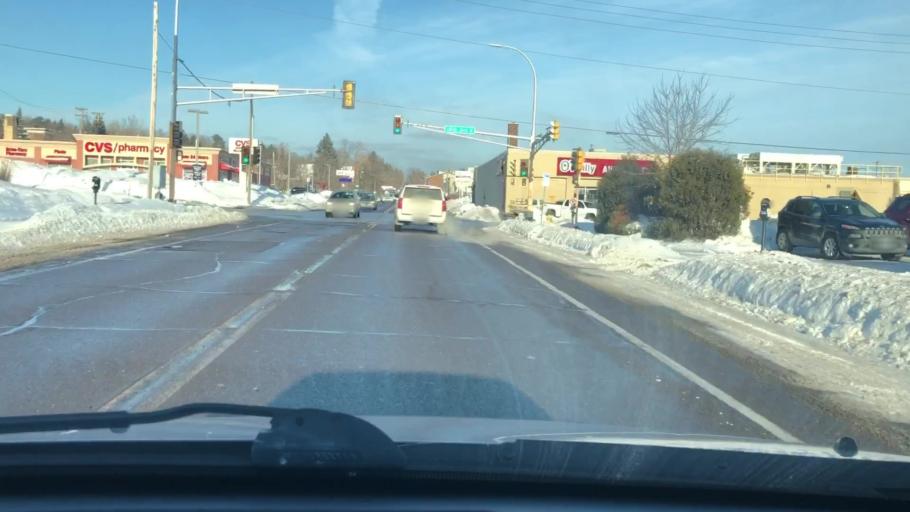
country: US
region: Minnesota
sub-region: Saint Louis County
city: Duluth
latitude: 46.7980
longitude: -92.0837
